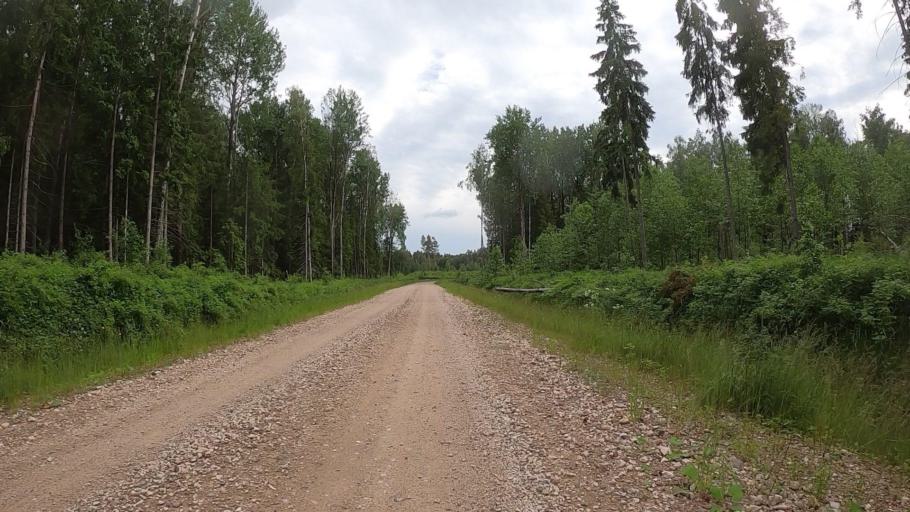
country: LV
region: Olaine
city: Olaine
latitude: 56.7593
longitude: 23.8797
